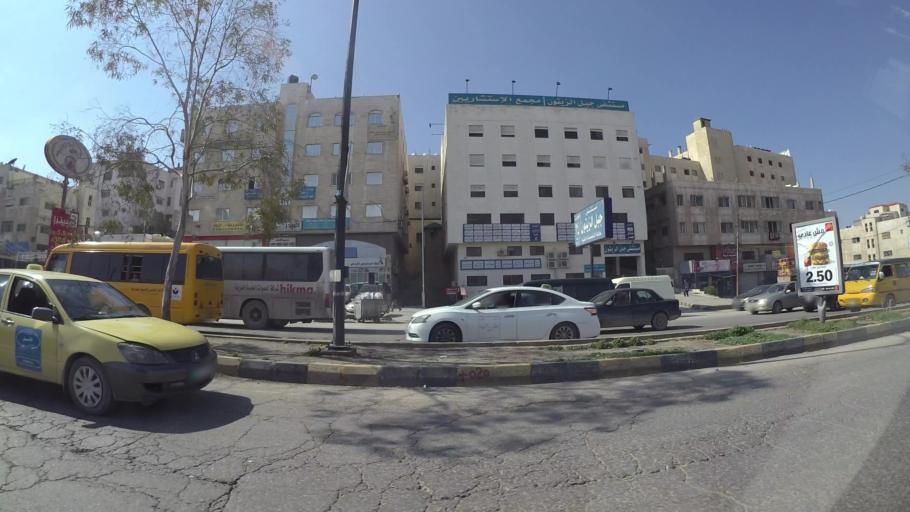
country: JO
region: Zarqa
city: Zarqa
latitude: 32.0375
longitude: 36.0923
